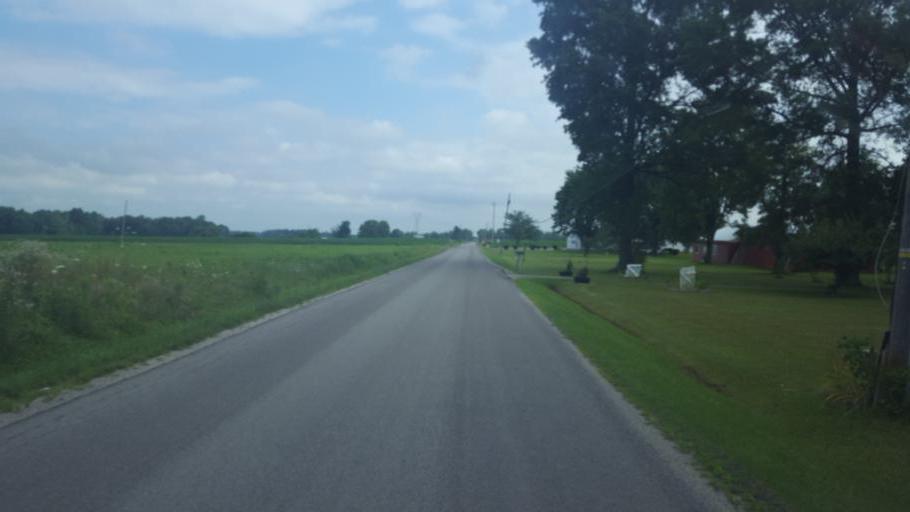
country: US
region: Ohio
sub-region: Crawford County
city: Galion
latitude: 40.6835
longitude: -82.7841
